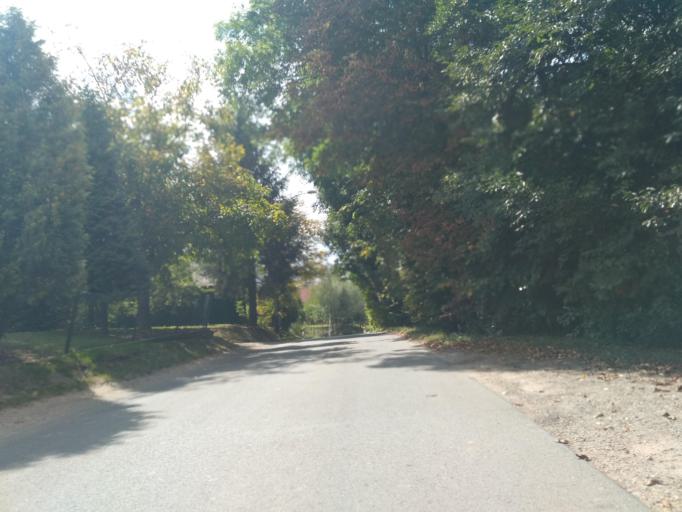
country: PL
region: Subcarpathian Voivodeship
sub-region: Powiat rzeszowski
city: Dynow
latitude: 49.8100
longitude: 22.2540
